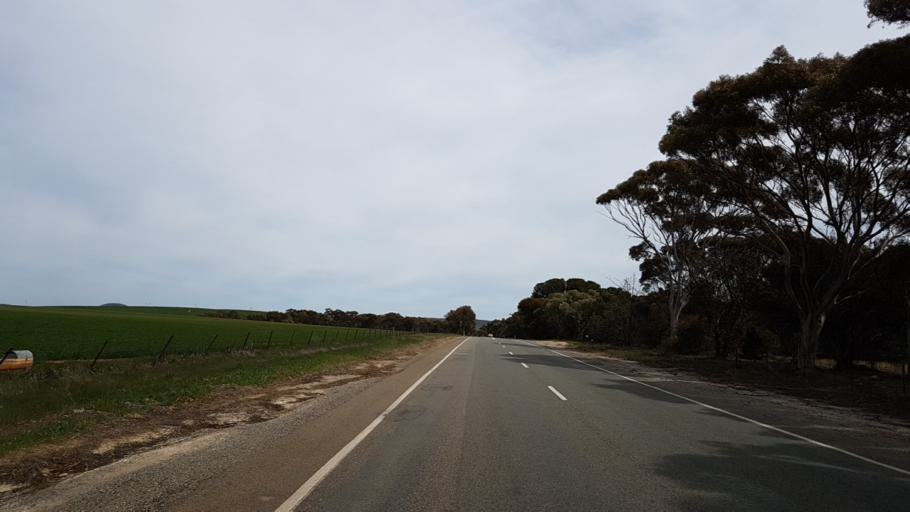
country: AU
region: South Australia
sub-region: Northern Areas
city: Jamestown
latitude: -33.0388
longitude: 138.6393
